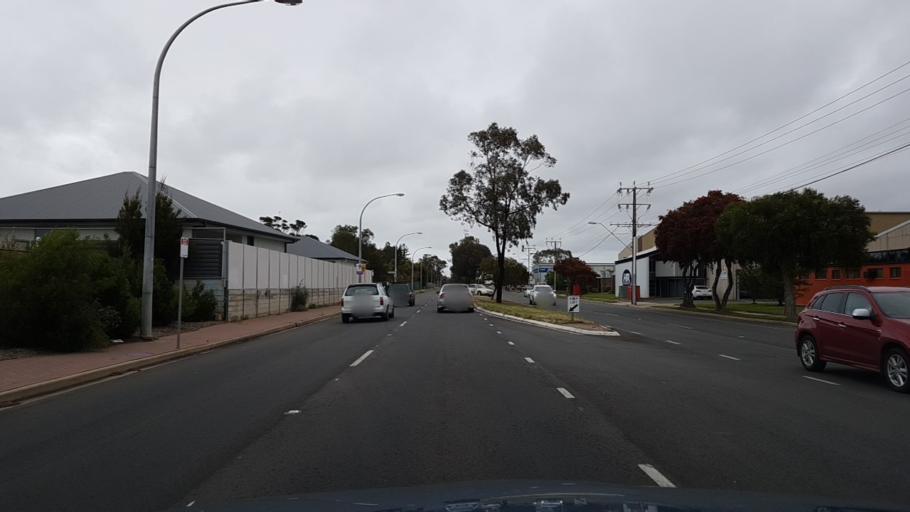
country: AU
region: South Australia
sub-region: Charles Sturt
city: Royal Park
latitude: -34.8687
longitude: 138.5030
